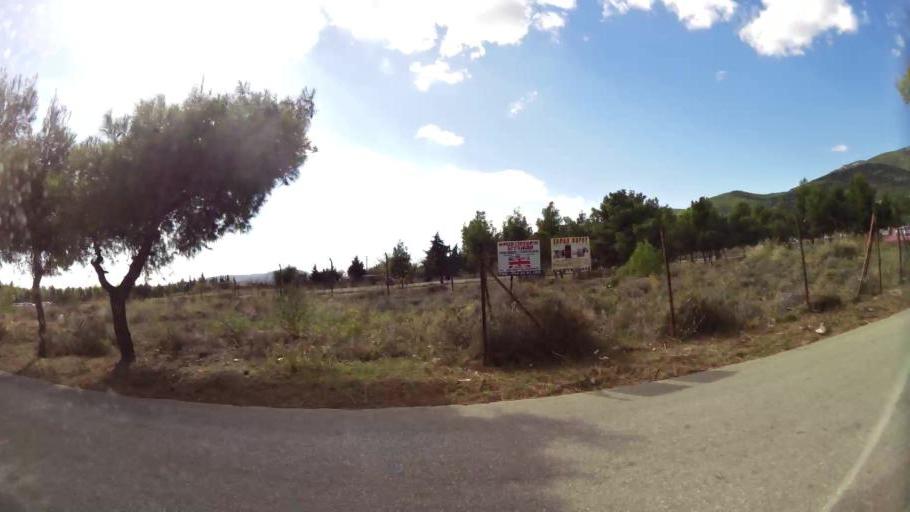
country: GR
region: Attica
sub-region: Nomarchia Anatolikis Attikis
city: Acharnes
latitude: 38.1095
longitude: 23.7324
